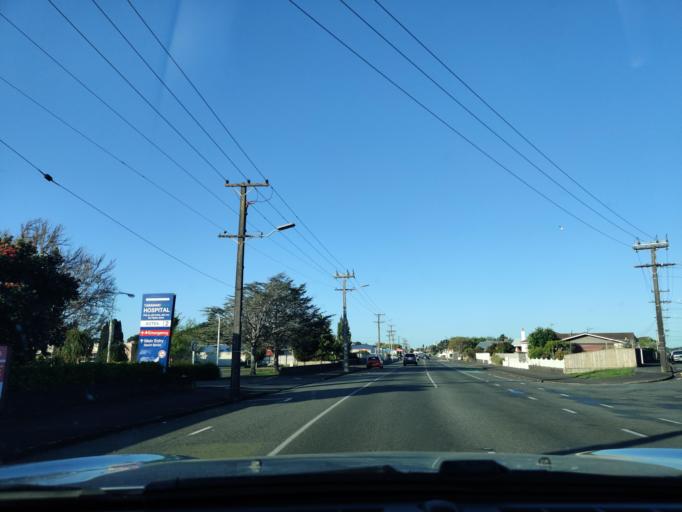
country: NZ
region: Taranaki
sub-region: New Plymouth District
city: New Plymouth
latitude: -39.0751
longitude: 174.0573
